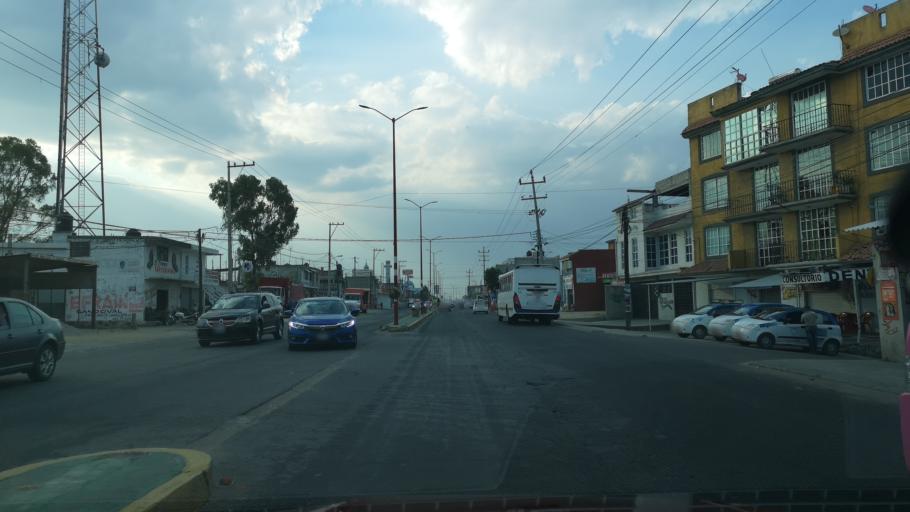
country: MX
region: Puebla
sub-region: Juan C. Bonilla
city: Santa Maria Zacatepec
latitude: 19.1201
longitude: -98.3628
